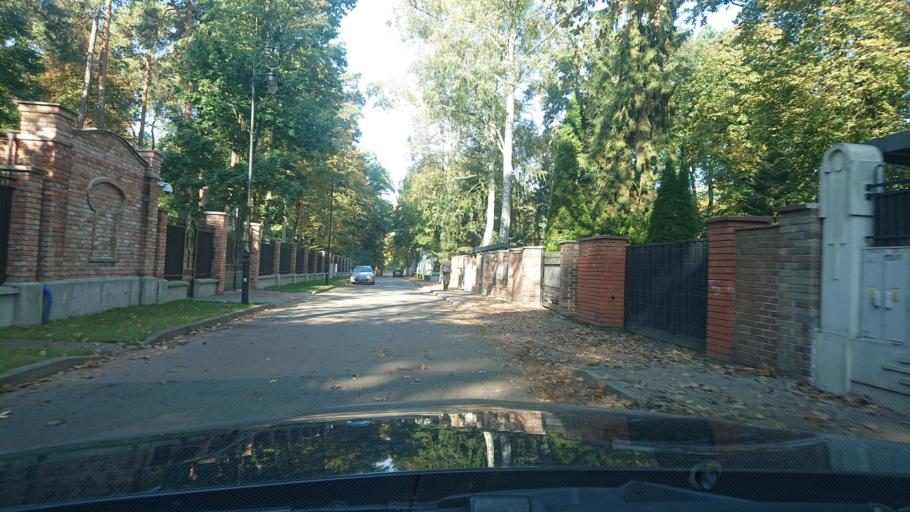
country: PL
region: Masovian Voivodeship
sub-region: Powiat piaseczynski
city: Konstancin-Jeziorna
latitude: 52.0802
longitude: 21.1225
